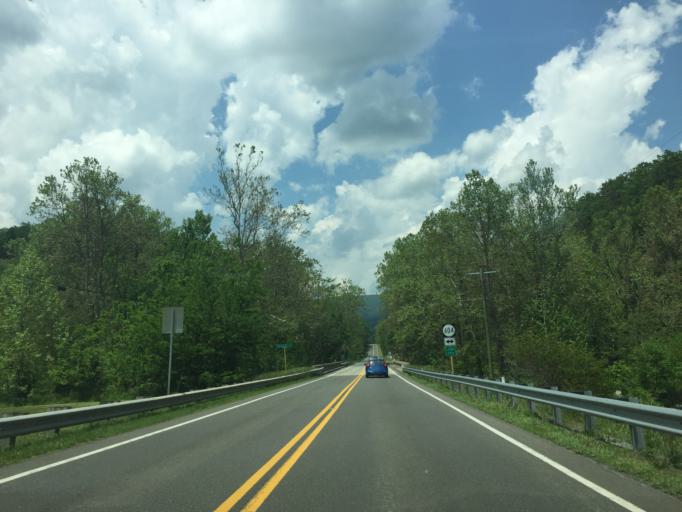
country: US
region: Virginia
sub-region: Shenandoah County
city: Strasburg
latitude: 39.0810
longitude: -78.4243
